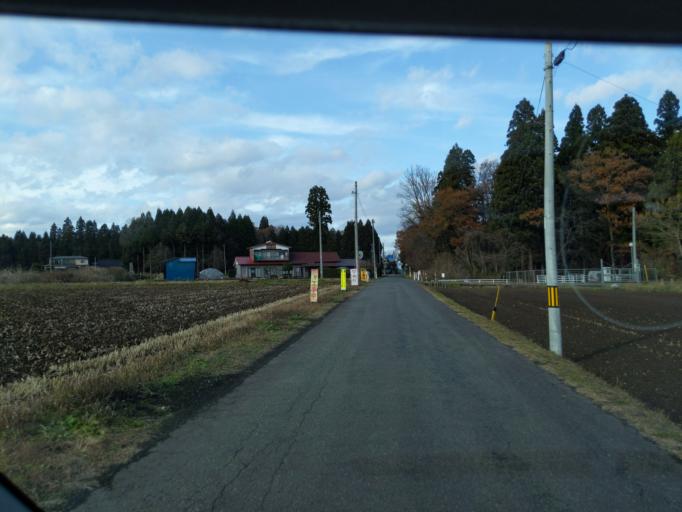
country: JP
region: Iwate
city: Mizusawa
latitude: 39.1154
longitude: 141.0921
